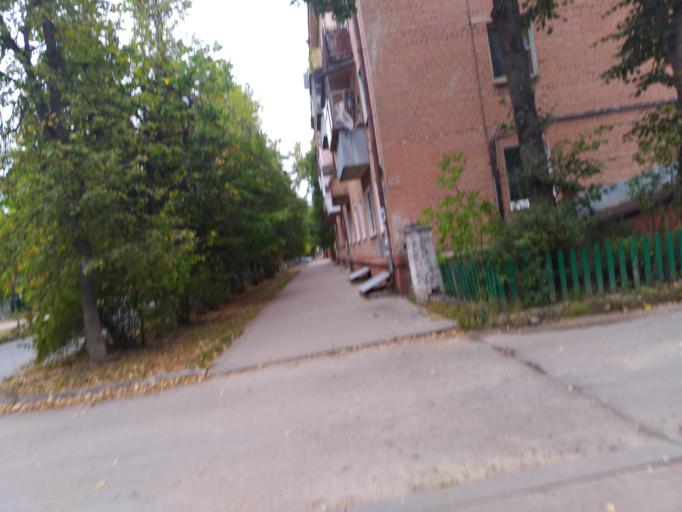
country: RU
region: Kaluga
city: Kaluga
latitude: 54.5323
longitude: 36.2589
